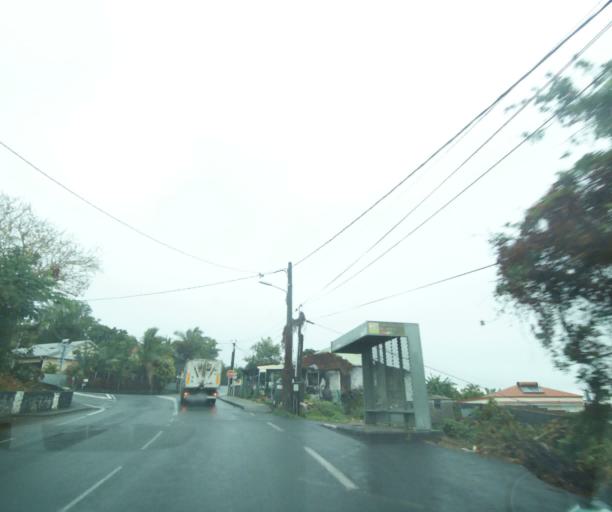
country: RE
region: Reunion
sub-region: Reunion
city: Saint-Paul
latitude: -21.0221
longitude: 55.2880
